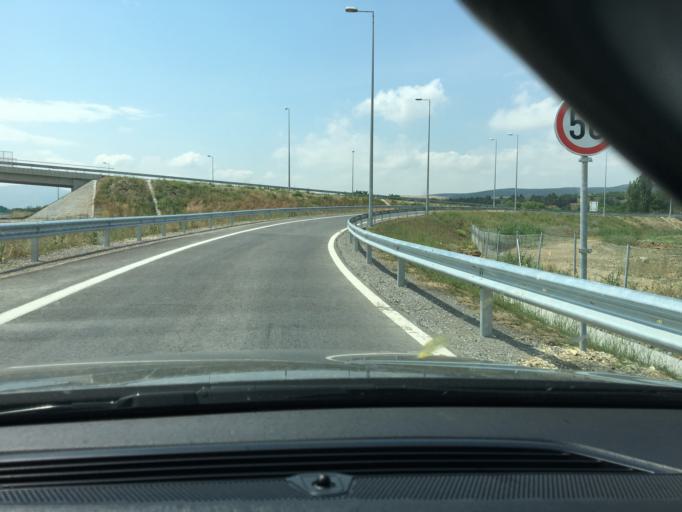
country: MK
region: Sveti Nikole
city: Sveti Nikole
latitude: 41.8564
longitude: 21.9620
